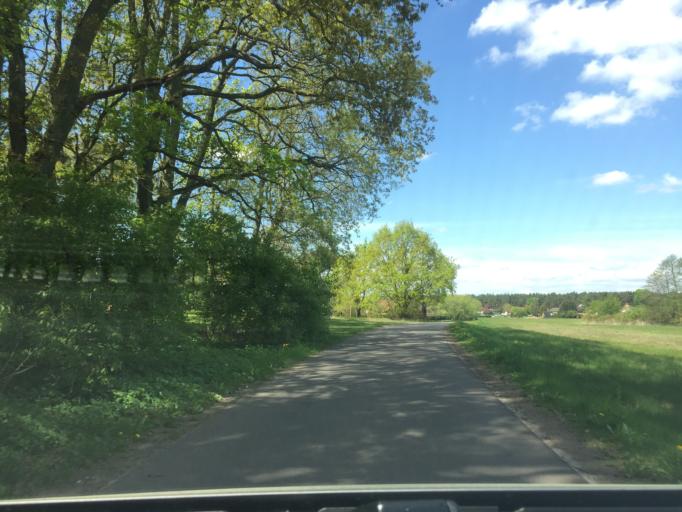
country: DE
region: Mecklenburg-Vorpommern
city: Torgelow
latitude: 53.6220
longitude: 13.9990
